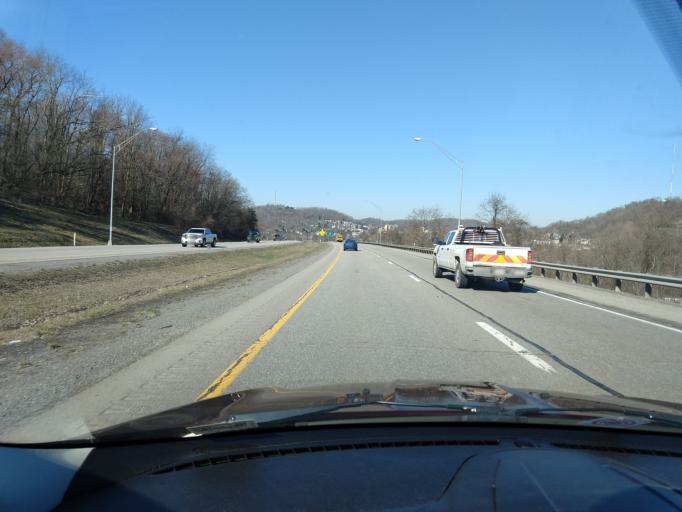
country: US
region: West Virginia
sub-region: Harrison County
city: Despard
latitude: 39.2775
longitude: -80.3131
